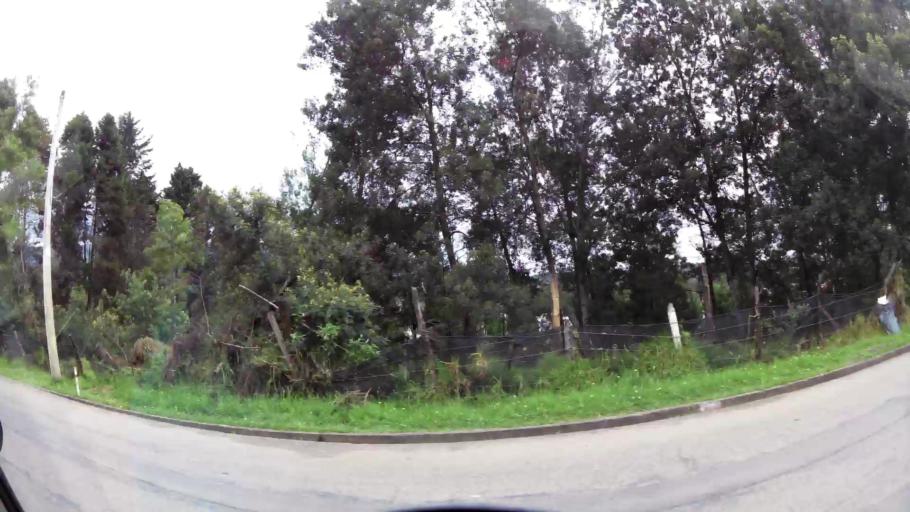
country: EC
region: Azuay
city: Cuenca
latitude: -2.8838
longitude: -79.0689
